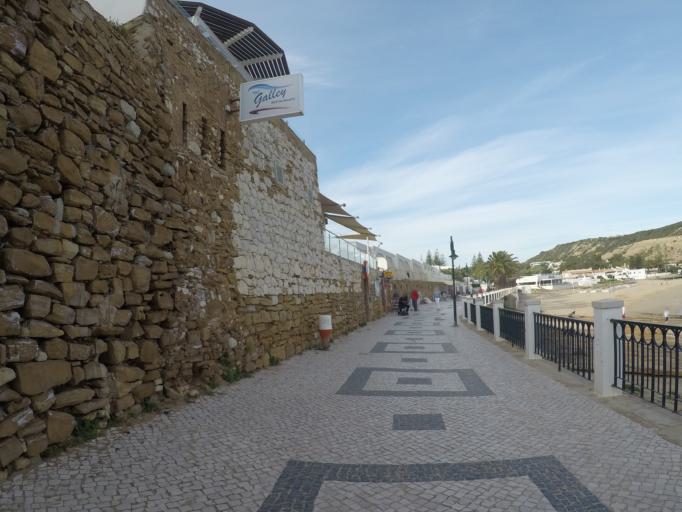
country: PT
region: Faro
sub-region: Lagos
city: Lagos
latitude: 37.0863
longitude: -8.7284
